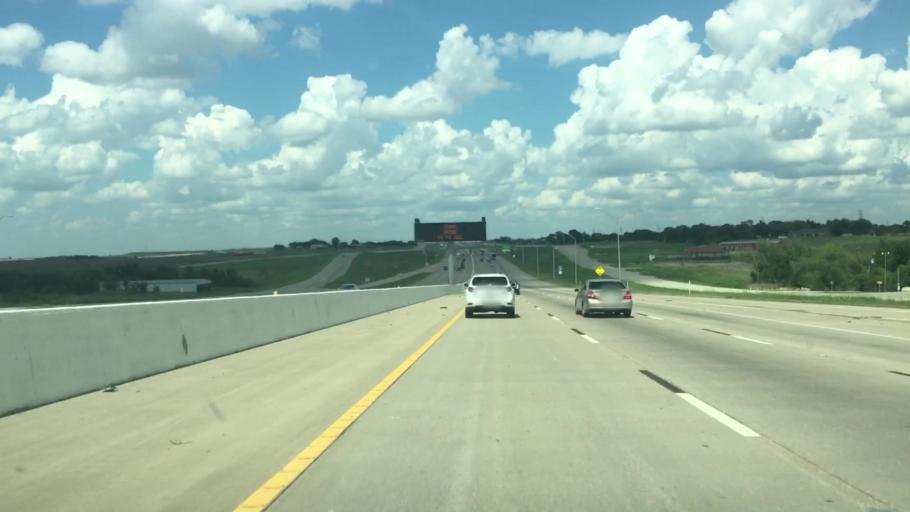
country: US
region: Texas
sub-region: McLennan County
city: West
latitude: 31.8323
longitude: -97.0926
